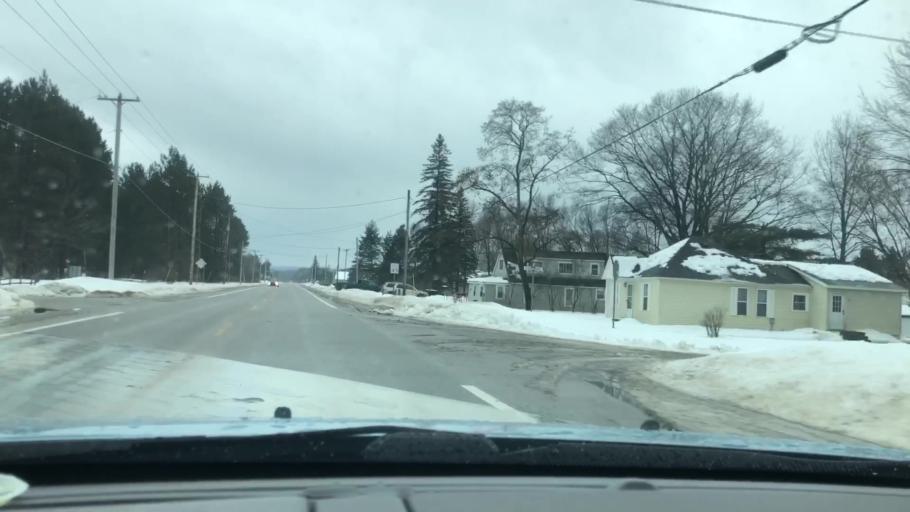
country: US
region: Michigan
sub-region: Charlevoix County
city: East Jordan
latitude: 45.1434
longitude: -85.1192
